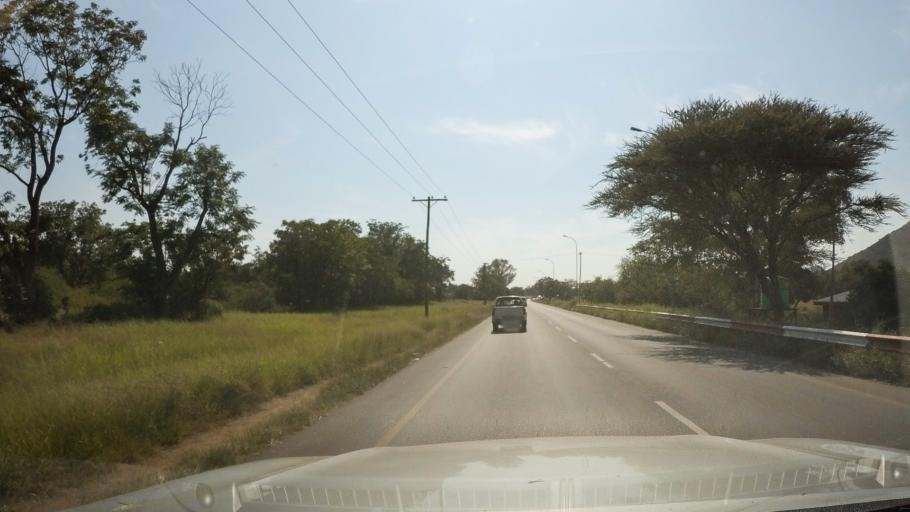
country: BW
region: South East
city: Lobatse
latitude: -25.2187
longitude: 25.6804
